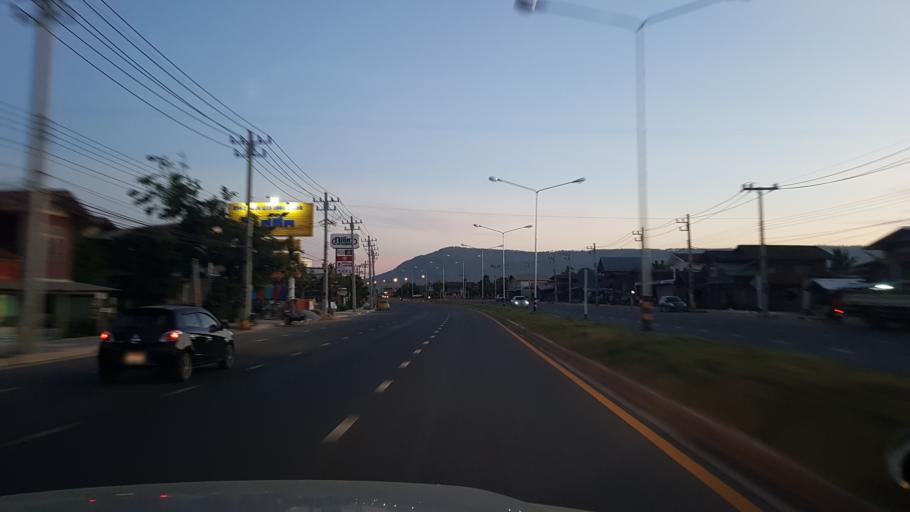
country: TH
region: Chaiyaphum
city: Phu Khiao
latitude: 16.3592
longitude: 102.1492
